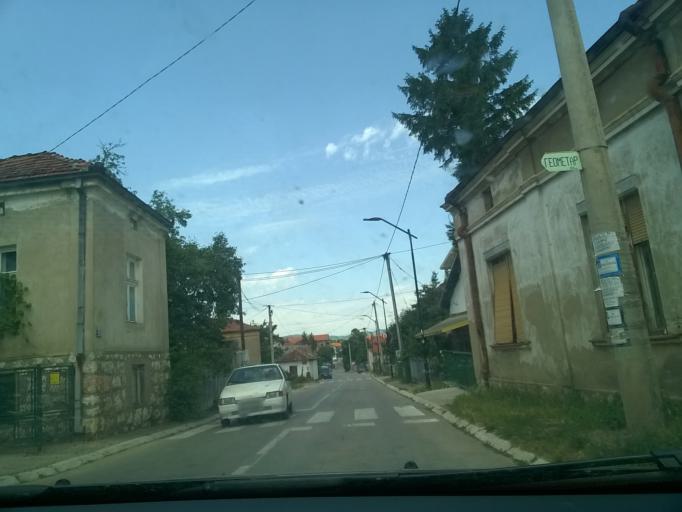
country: RS
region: Central Serbia
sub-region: Zajecarski Okrug
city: Soko Banja
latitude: 43.6449
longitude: 21.8666
